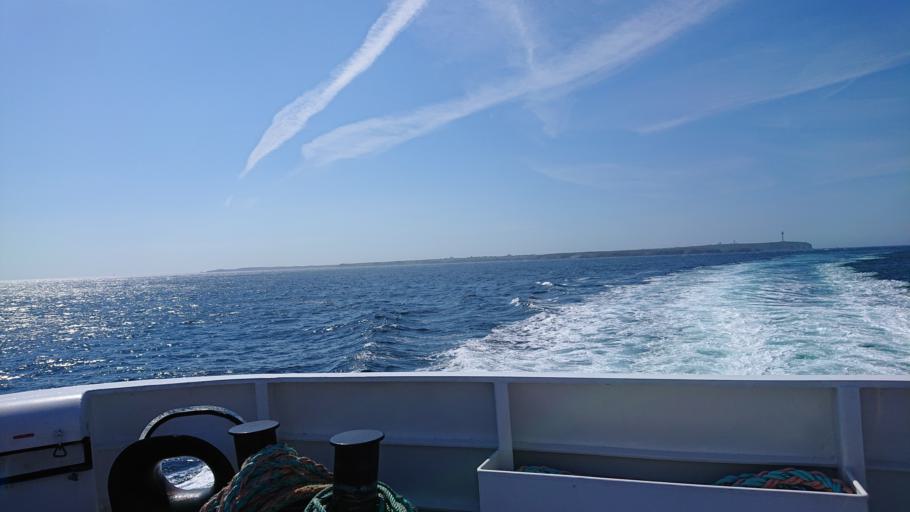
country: FR
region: Brittany
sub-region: Departement du Finistere
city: Porspoder
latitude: 48.4481
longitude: -5.0024
